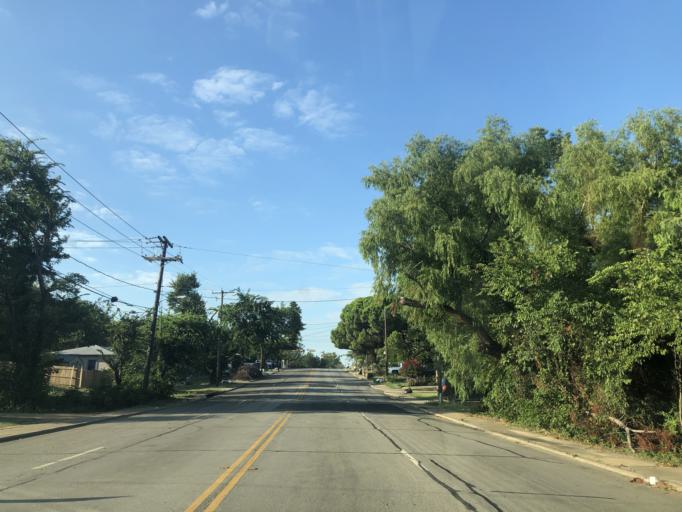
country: US
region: Texas
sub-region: Dallas County
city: Grand Prairie
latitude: 32.7466
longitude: -97.0288
